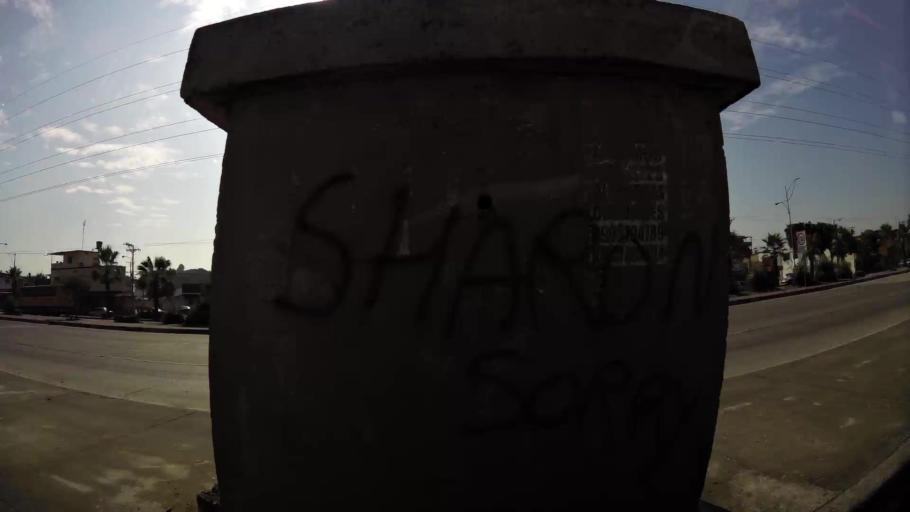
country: EC
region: Guayas
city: Eloy Alfaro
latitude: -2.0856
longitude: -79.9146
